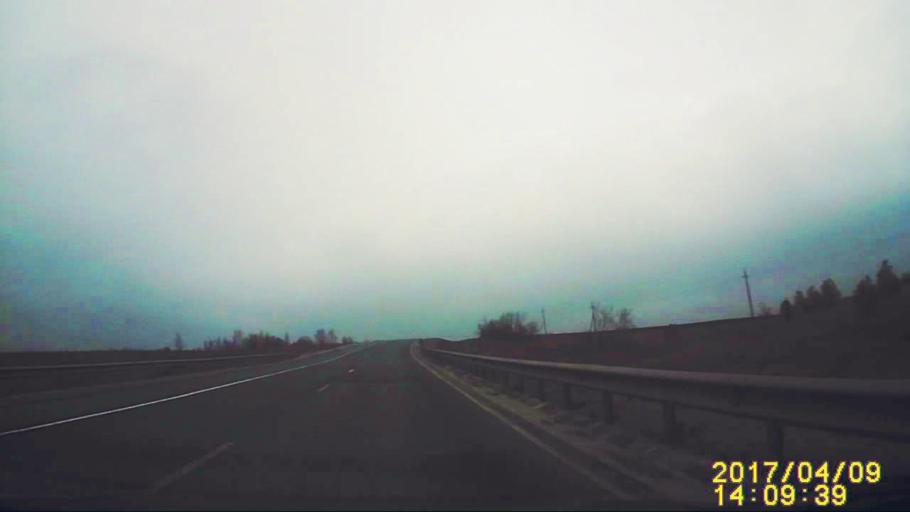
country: RU
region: Ulyanovsk
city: Krasnyy Gulyay
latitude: 54.0307
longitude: 48.2128
